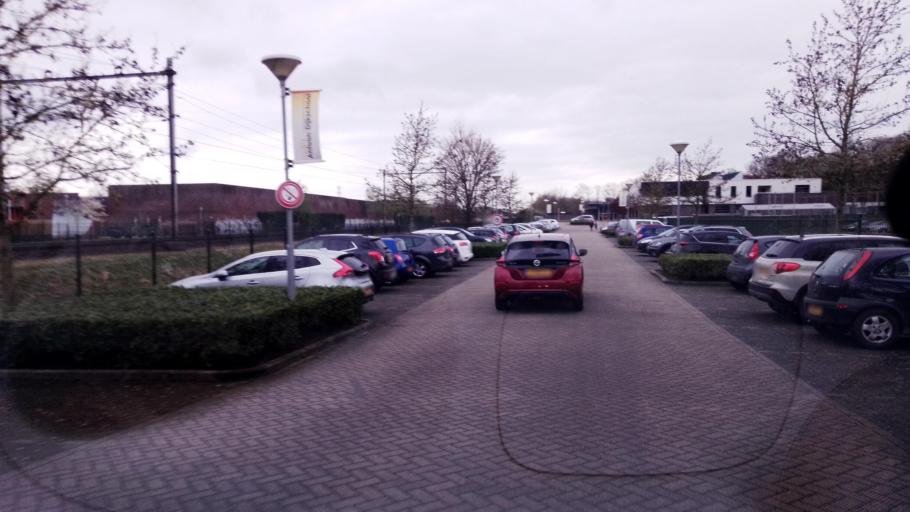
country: NL
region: North Brabant
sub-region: Gemeente Helmond
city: Helmond
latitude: 51.4693
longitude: 5.7113
